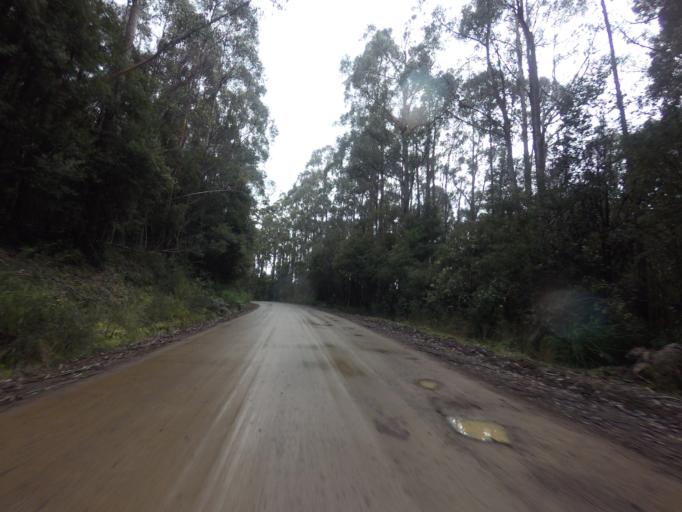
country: AU
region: Tasmania
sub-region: Huon Valley
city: Geeveston
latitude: -43.4835
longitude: 146.8921
